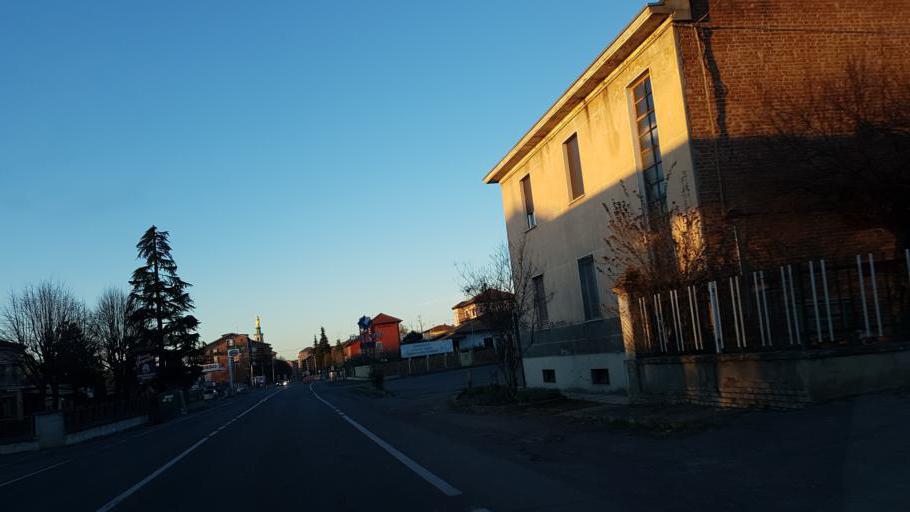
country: IT
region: Piedmont
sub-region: Provincia di Alessandria
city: Tortona
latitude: 44.8811
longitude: 8.8584
